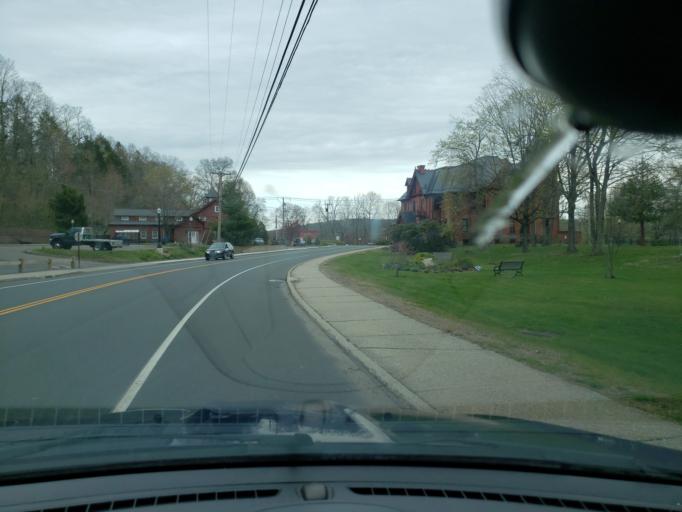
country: US
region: Connecticut
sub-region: New Haven County
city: Naugatuck
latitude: 41.4945
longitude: -73.0555
